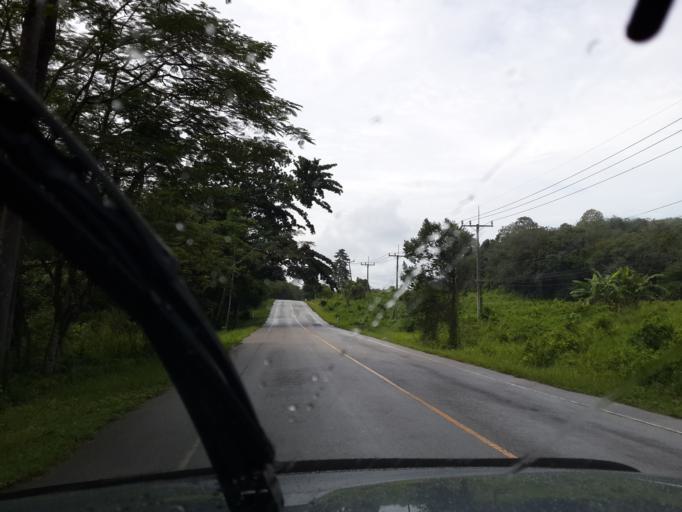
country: TH
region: Narathiwat
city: Rueso
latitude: 6.3687
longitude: 101.5332
